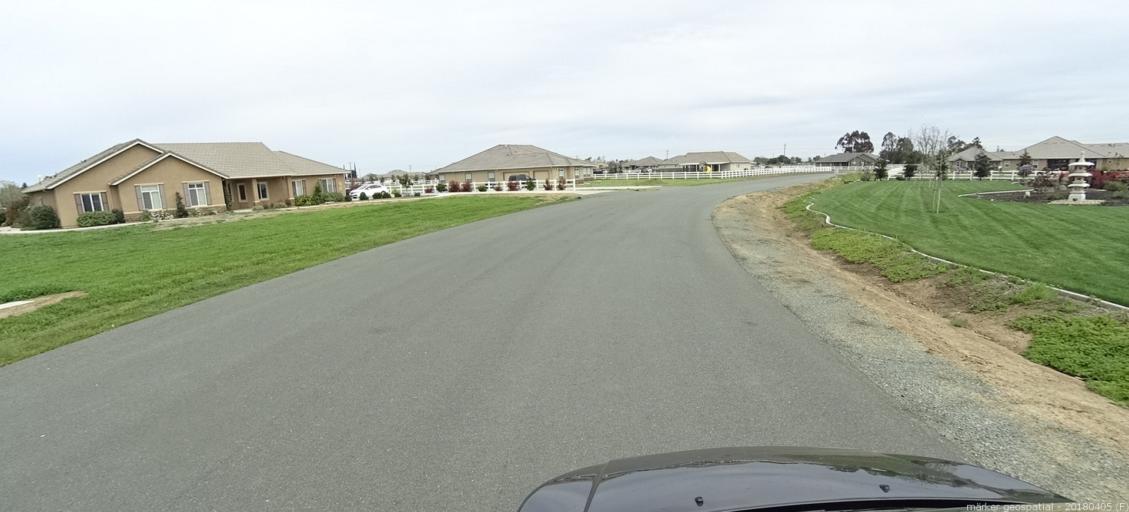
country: US
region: California
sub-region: Sacramento County
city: Galt
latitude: 38.2854
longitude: -121.3230
